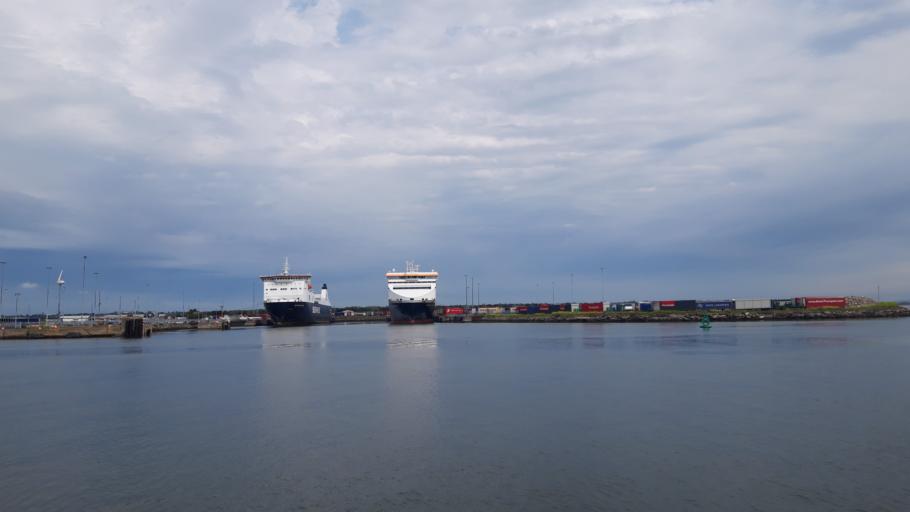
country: IE
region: Leinster
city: Sandymount
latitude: 53.3432
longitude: -6.1917
